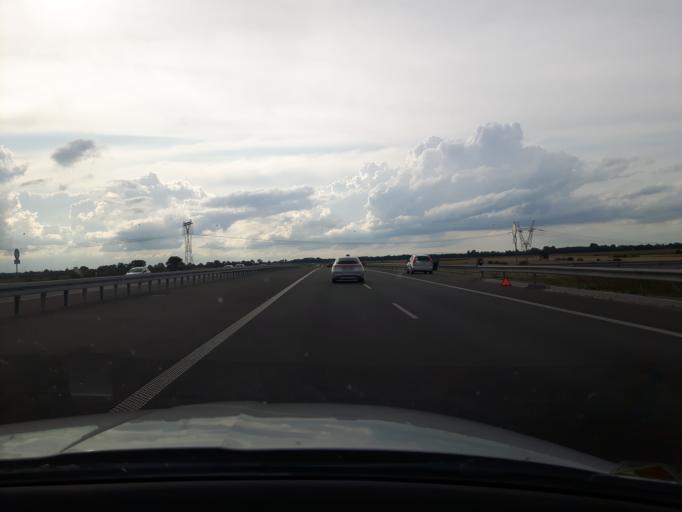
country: PL
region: Warmian-Masurian Voivodeship
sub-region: Powiat elblaski
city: Gronowo Elblaskie
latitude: 54.1665
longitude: 19.2377
